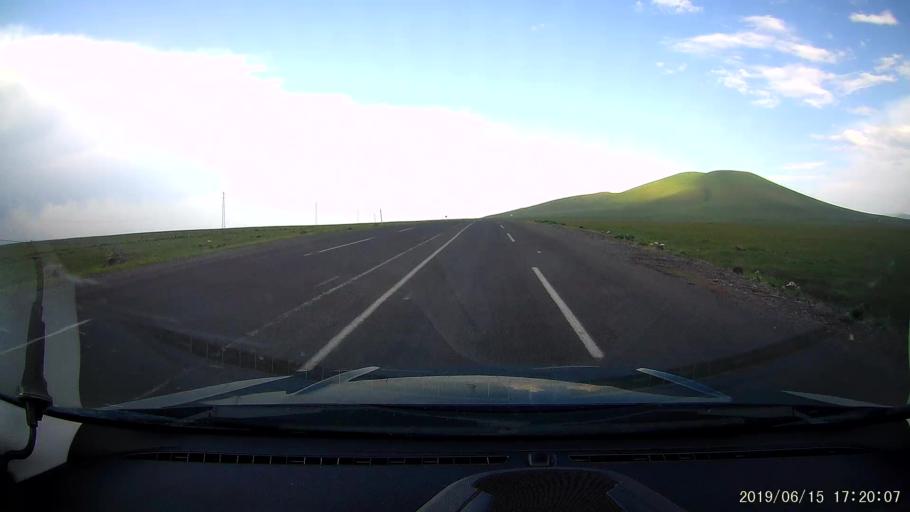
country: TR
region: Kars
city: Kars
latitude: 40.6161
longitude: 43.2936
